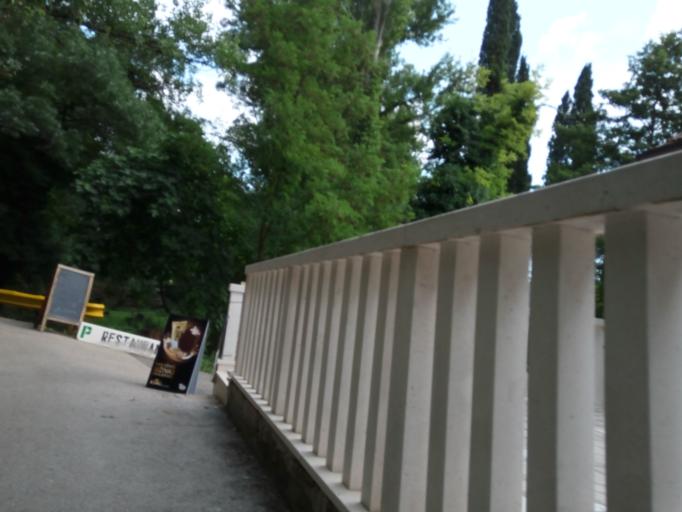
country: HR
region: Sibensko-Kniniska
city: Kistanje
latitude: 43.9049
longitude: 15.9767
